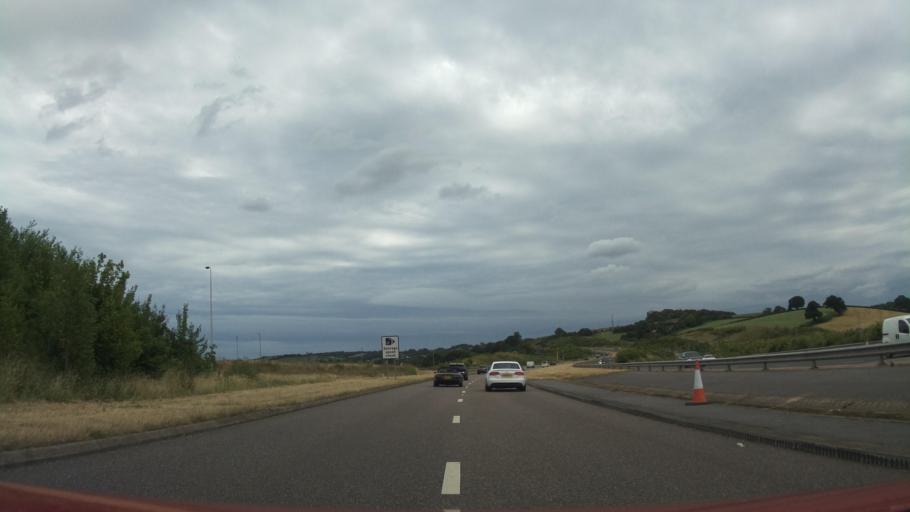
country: GB
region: England
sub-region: Devon
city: Kingskerswell
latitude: 50.5125
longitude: -3.5876
